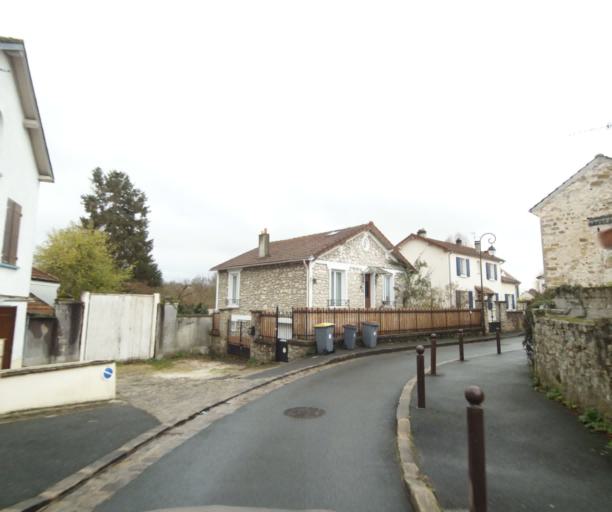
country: FR
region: Ile-de-France
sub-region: Departement de Seine-et-Marne
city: Avon
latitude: 48.4165
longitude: 2.7318
